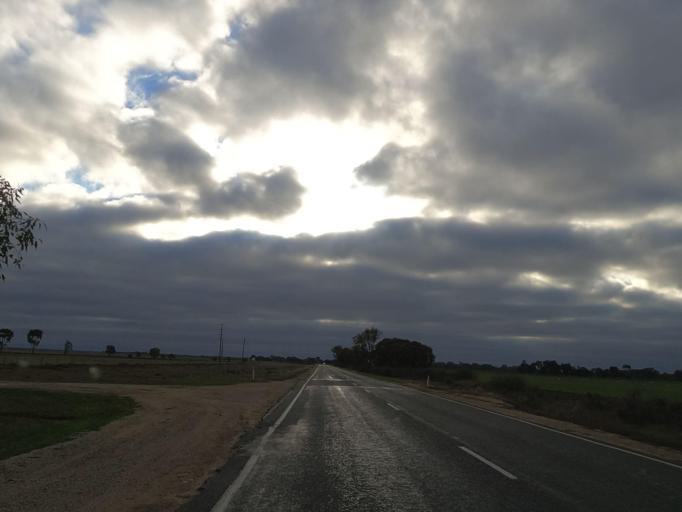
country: AU
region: Victoria
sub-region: Swan Hill
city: Swan Hill
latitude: -35.6554
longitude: 143.8502
